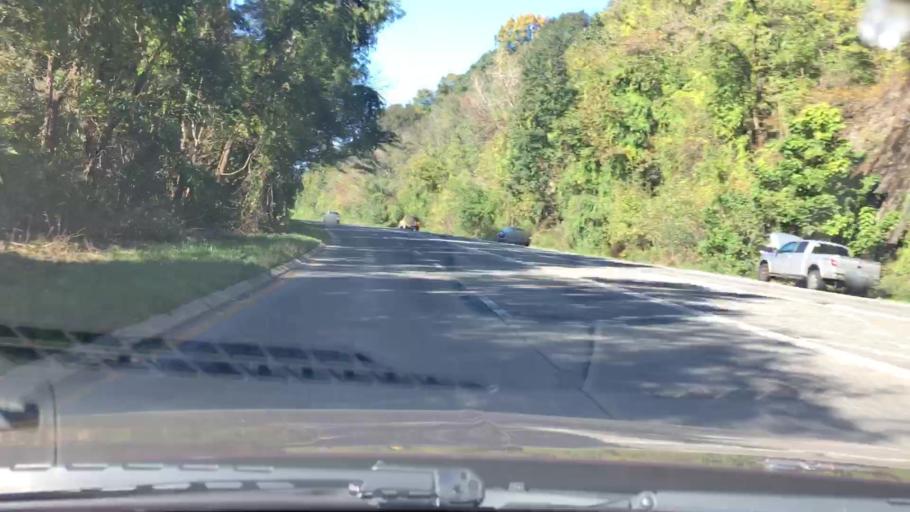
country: US
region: New York
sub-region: Westchester County
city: Katonah
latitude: 41.2545
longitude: -73.6766
